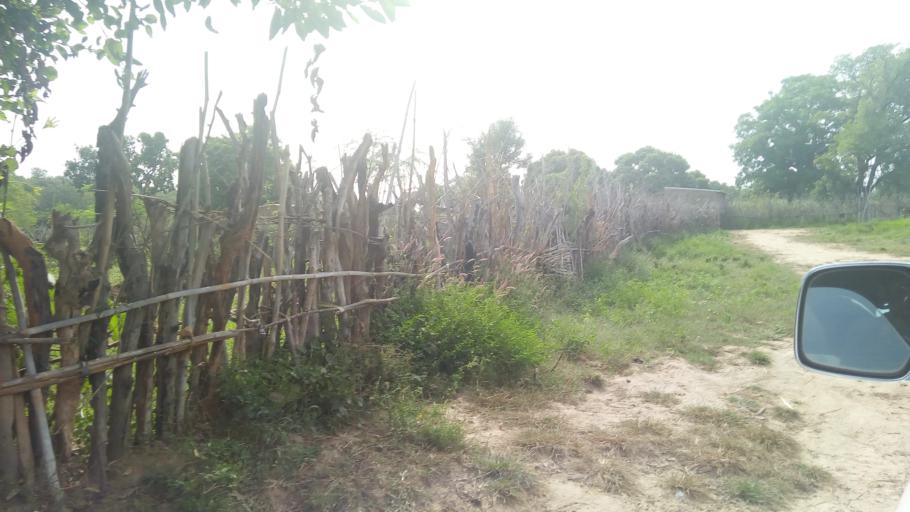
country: ML
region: Kayes
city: Kita
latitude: 13.1349
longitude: -8.8333
